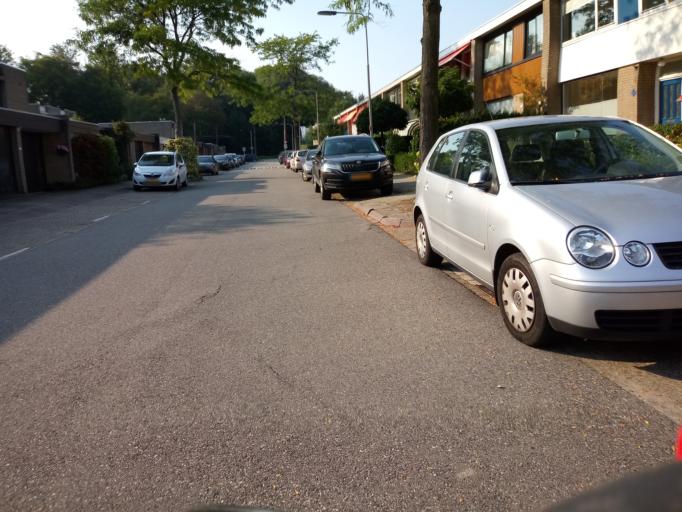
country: NL
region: Gelderland
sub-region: Gemeente Rozendaal
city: Rozendaal
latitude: 51.9885
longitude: 5.9528
